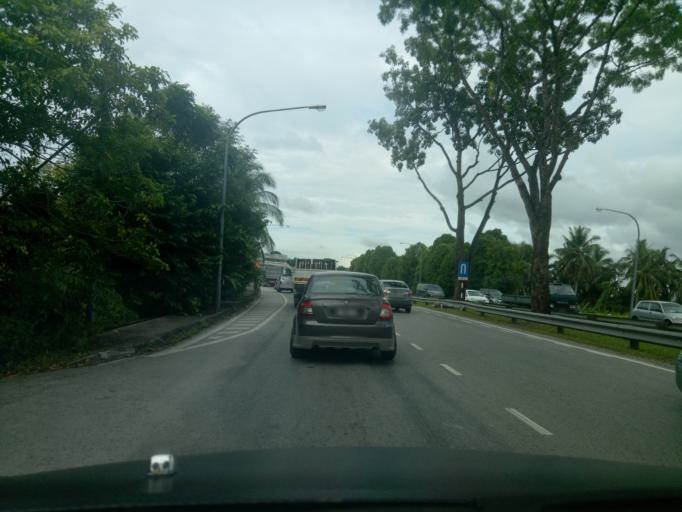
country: MY
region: Sarawak
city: Kuching
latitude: 1.5458
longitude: 110.3806
